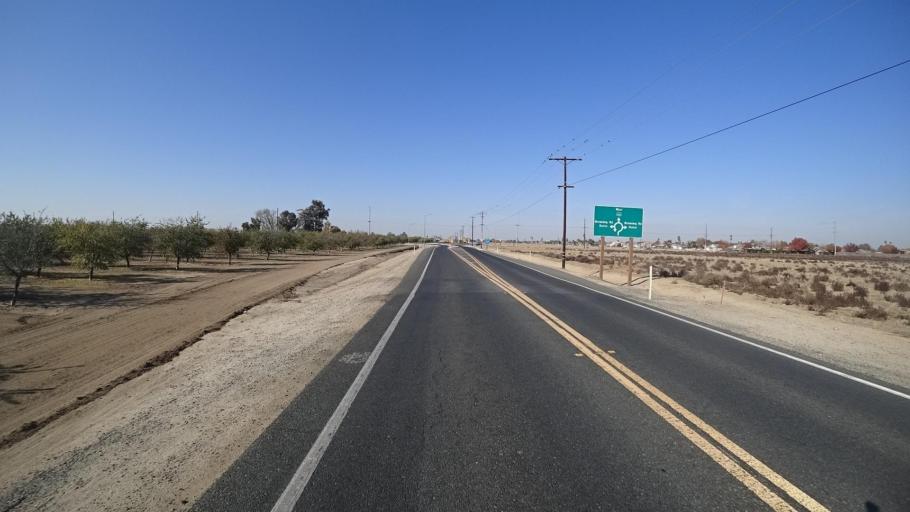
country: US
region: California
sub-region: Kern County
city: Delano
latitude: 35.7613
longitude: -119.2211
